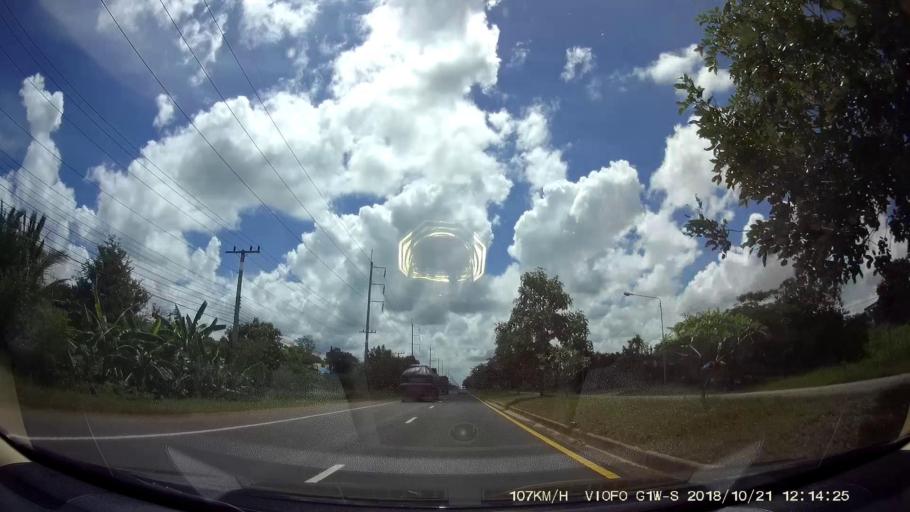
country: TH
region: Nakhon Ratchasima
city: Dan Khun Thot
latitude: 15.3777
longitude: 101.8352
